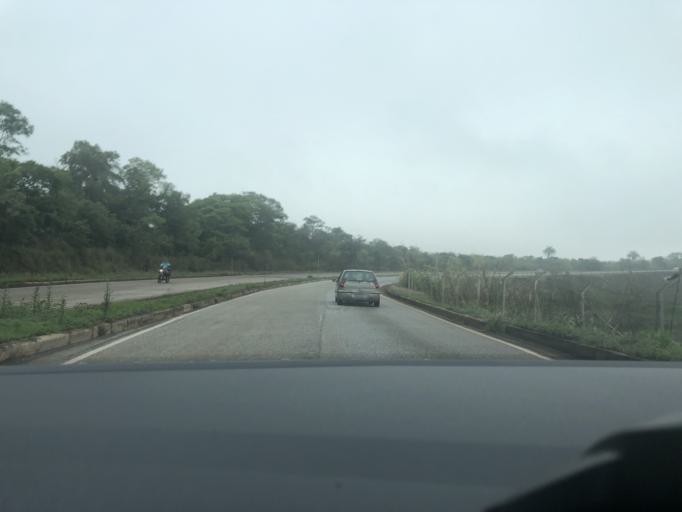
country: BR
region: Minas Gerais
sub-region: Congonhas
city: Congonhas
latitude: -20.5944
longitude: -43.9477
